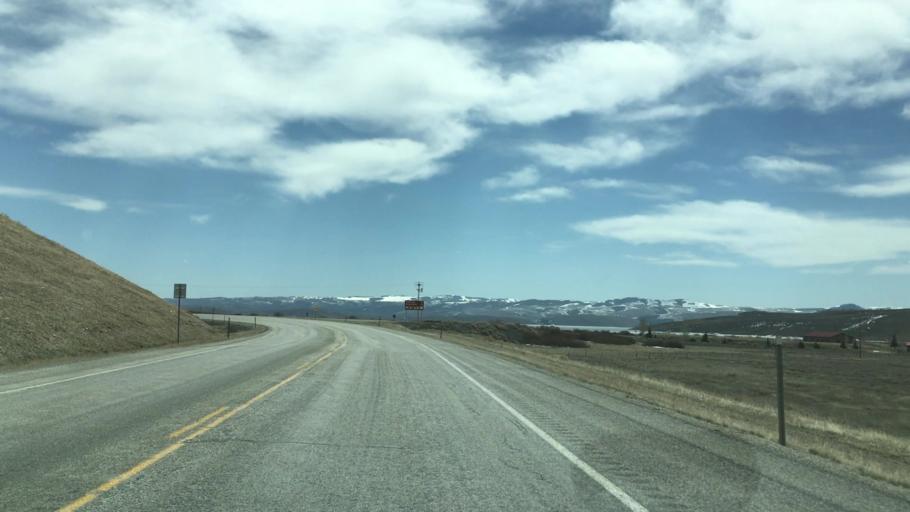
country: US
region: Utah
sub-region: Wasatch County
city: Heber
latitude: 40.2426
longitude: -111.1853
